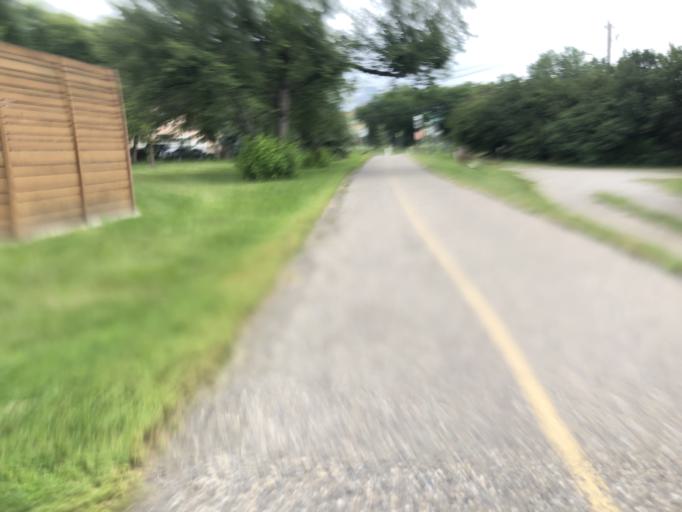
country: CA
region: Alberta
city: Calgary
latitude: 51.0411
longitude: -114.0284
